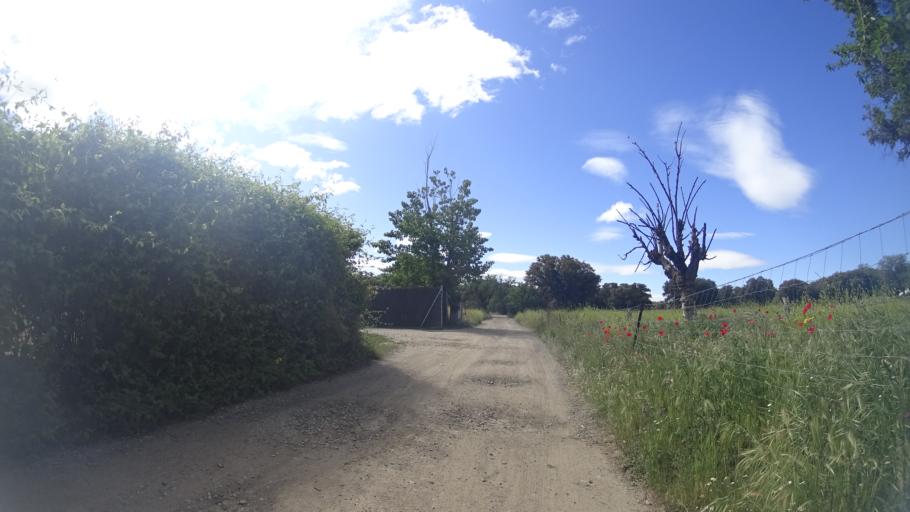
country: ES
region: Madrid
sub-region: Provincia de Madrid
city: Brunete
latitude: 40.4230
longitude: -3.9502
